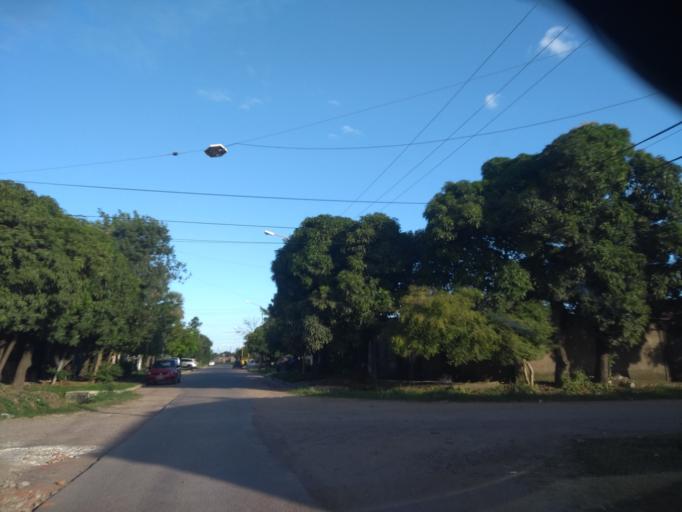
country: AR
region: Chaco
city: Barranqueras
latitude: -27.4862
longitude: -58.9435
